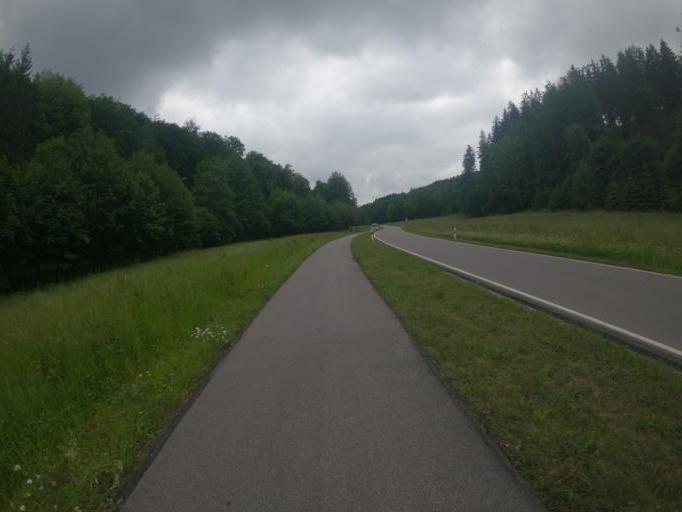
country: DE
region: Baden-Wuerttemberg
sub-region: Regierungsbezirk Stuttgart
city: Ebersbach an der Fils
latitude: 48.7369
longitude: 9.5463
